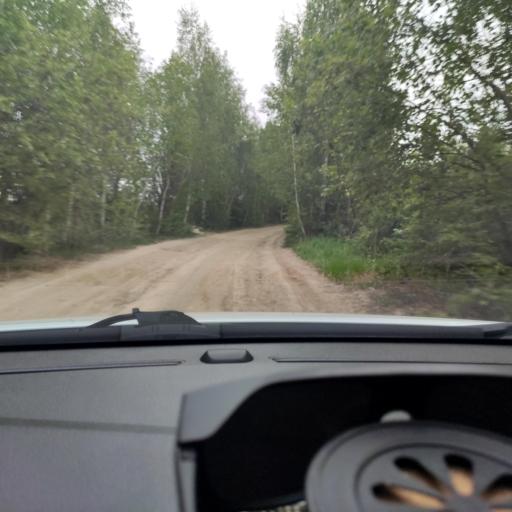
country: RU
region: Tatarstan
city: Vysokaya Gora
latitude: 55.8546
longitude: 49.2503
